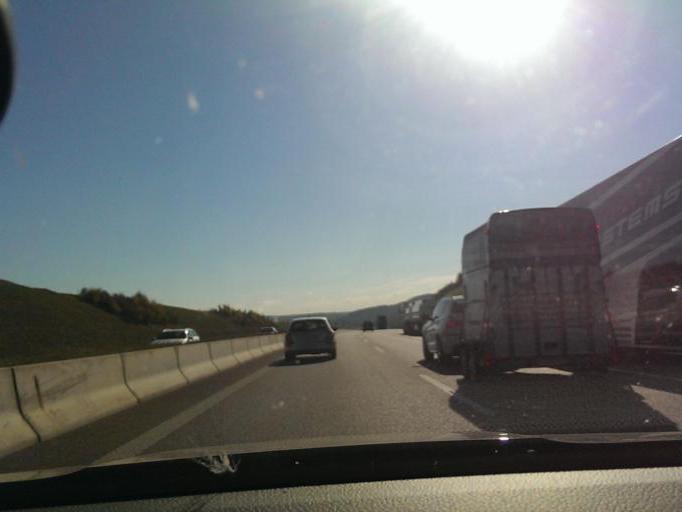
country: DE
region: Baden-Wuerttemberg
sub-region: Regierungsbezirk Stuttgart
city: Rutesheim
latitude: 48.7977
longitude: 8.9543
